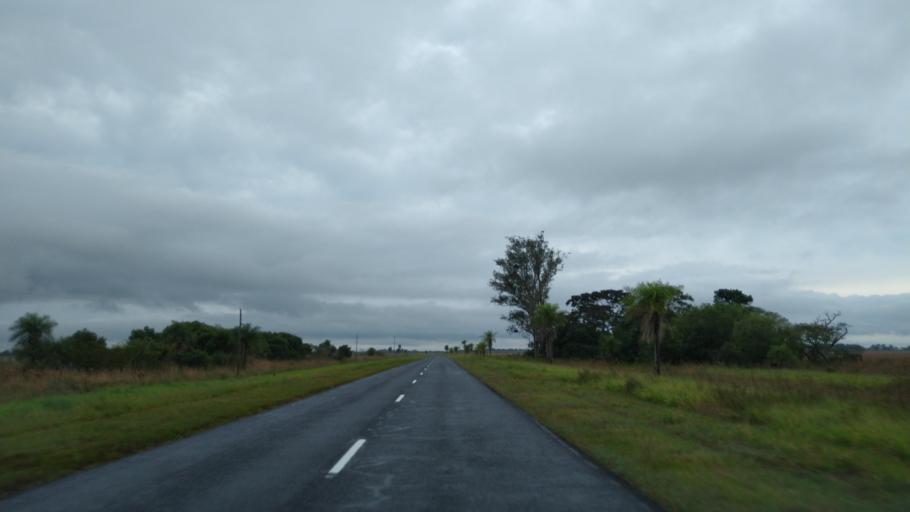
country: AR
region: Corrientes
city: Loreto
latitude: -27.7236
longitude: -57.2345
